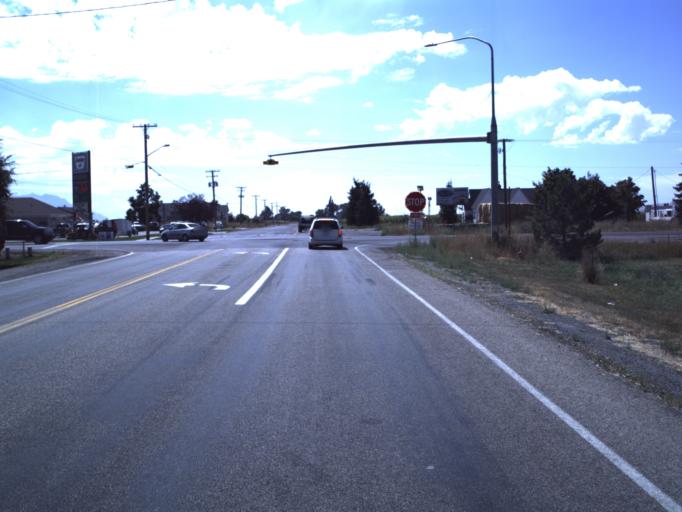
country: US
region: Utah
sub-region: Box Elder County
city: Garland
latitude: 41.7856
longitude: -112.1494
